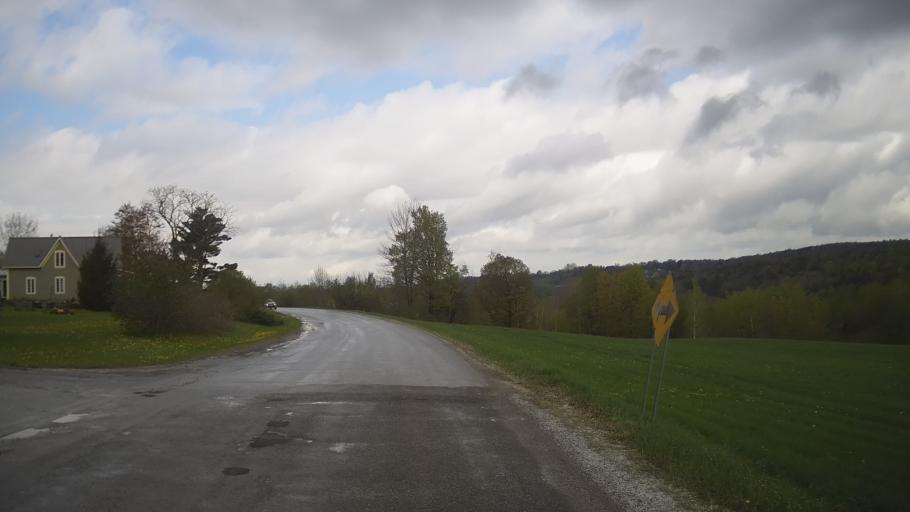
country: CA
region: Quebec
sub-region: Monteregie
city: Cowansville
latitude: 45.1957
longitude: -72.7043
